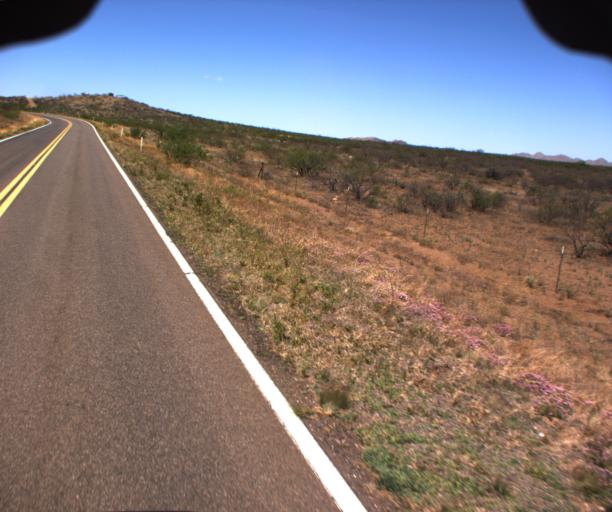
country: US
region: Arizona
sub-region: Cochise County
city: Douglas
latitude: 31.4908
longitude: -109.4259
